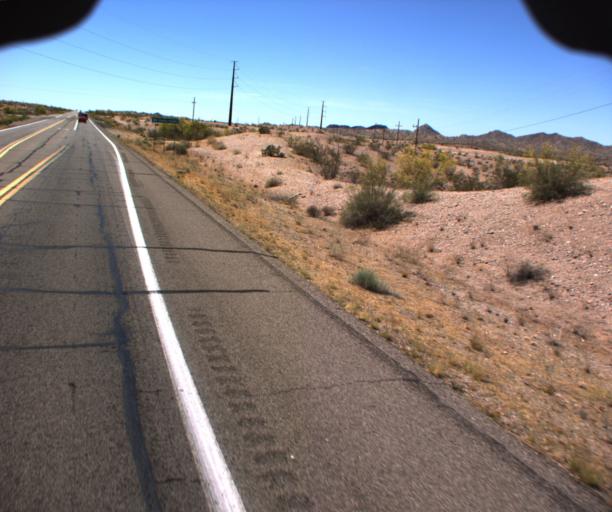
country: US
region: Arizona
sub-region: Mohave County
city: Desert Hills
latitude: 34.6644
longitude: -114.3135
